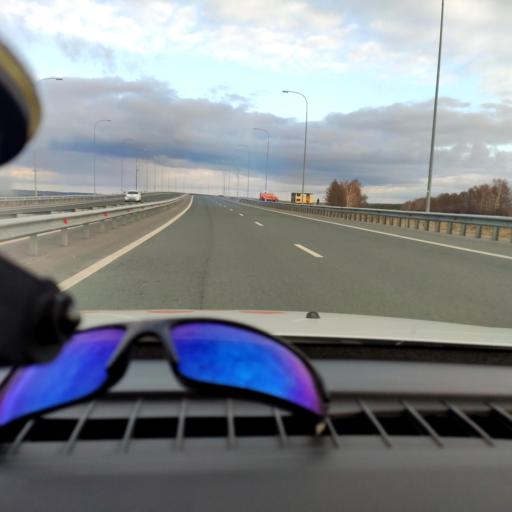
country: RU
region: Samara
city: Bereza
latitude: 53.4957
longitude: 50.1176
